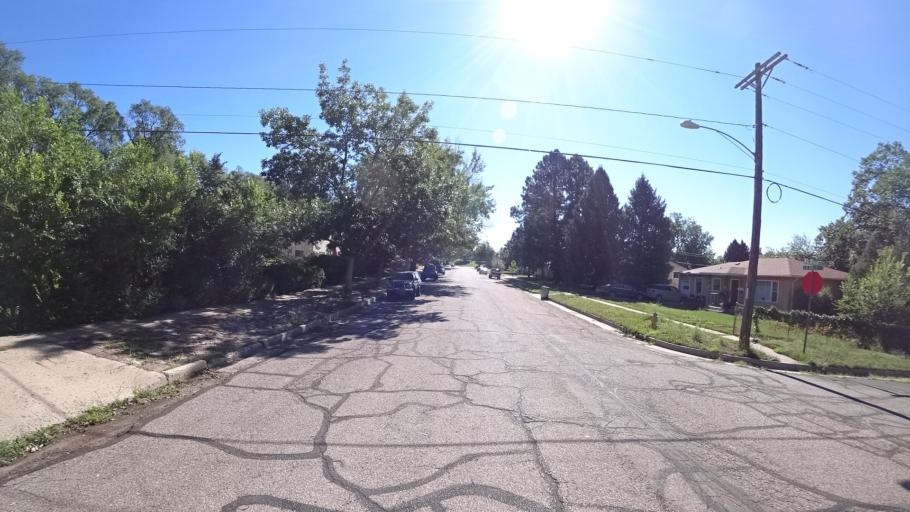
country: US
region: Colorado
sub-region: El Paso County
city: Colorado Springs
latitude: 38.8584
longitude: -104.7850
